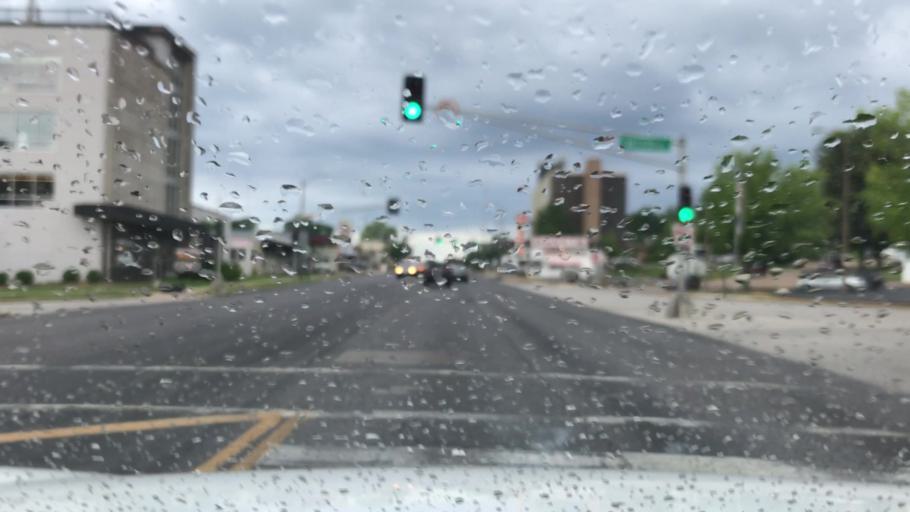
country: US
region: Missouri
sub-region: Saint Louis County
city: Maplewood
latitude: 38.5926
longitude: -90.3016
